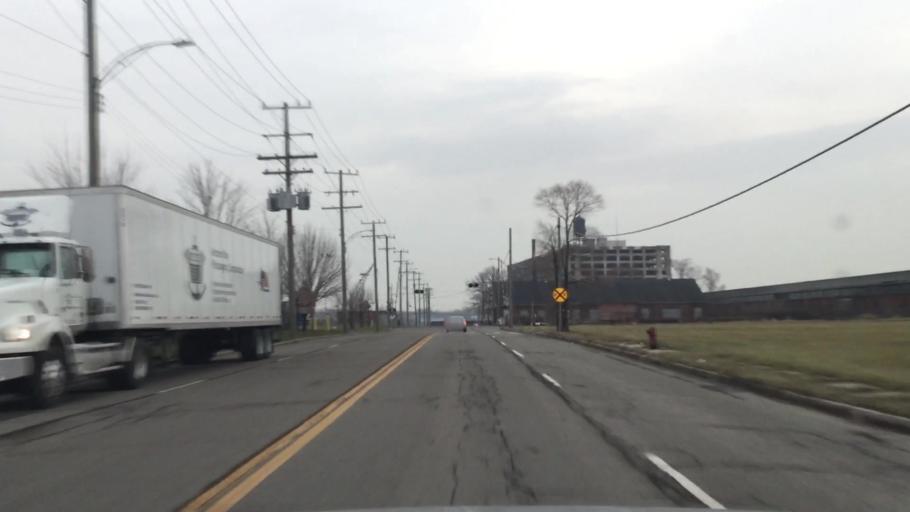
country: US
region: Michigan
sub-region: Wayne County
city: Detroit
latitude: 42.3108
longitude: -83.0891
